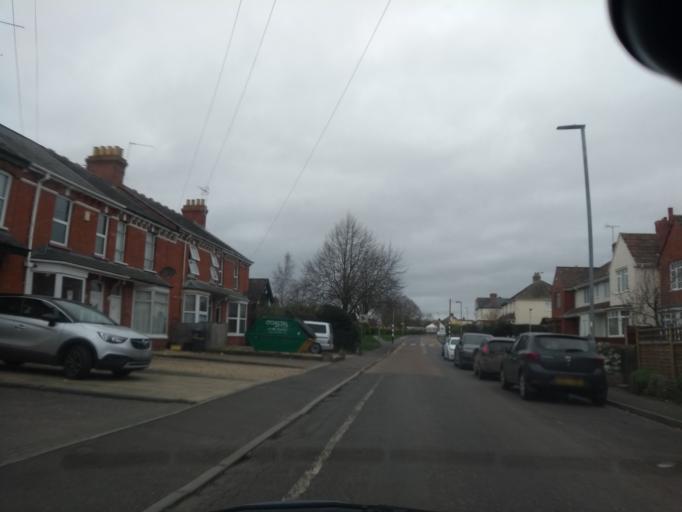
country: GB
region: England
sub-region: Somerset
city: Taunton
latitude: 51.0339
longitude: -3.1013
